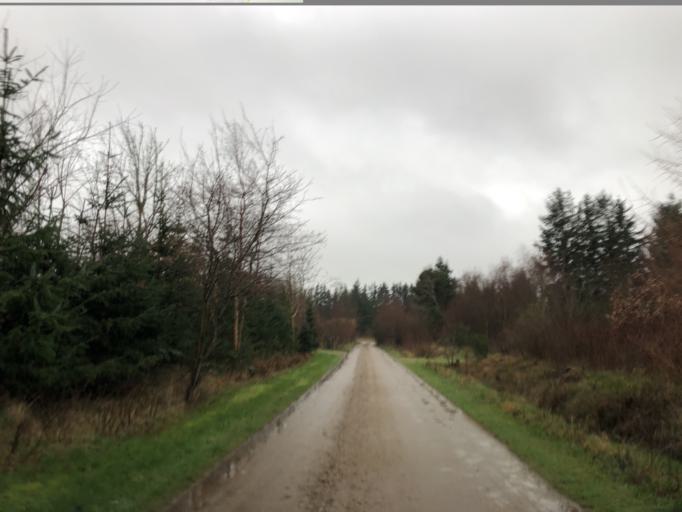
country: DK
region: Central Jutland
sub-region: Holstebro Kommune
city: Ulfborg
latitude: 56.2805
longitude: 8.1628
